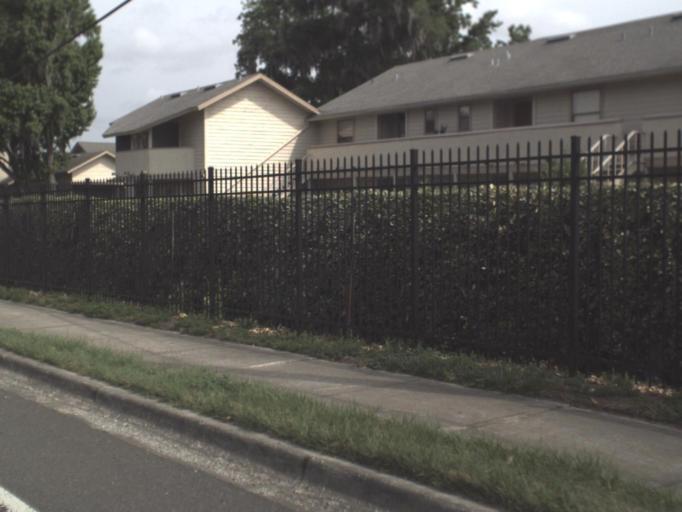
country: US
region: Florida
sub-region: Clay County
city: Green Cove Springs
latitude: 30.0059
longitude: -81.6898
